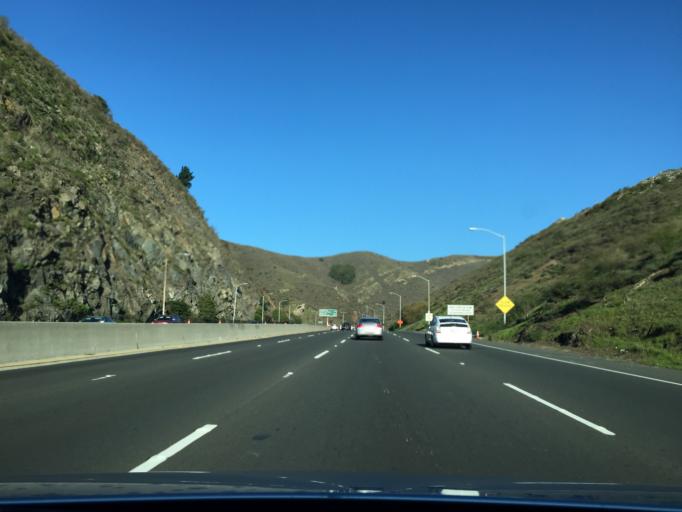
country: US
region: California
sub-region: Marin County
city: Sausalito
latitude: 37.8361
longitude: -122.4849
